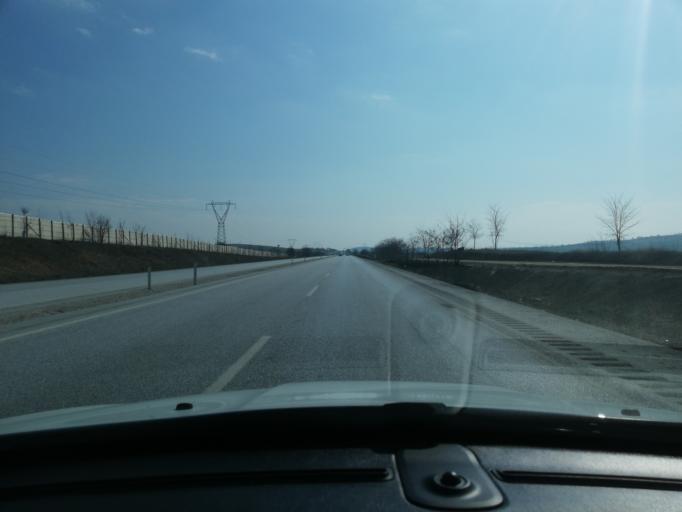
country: TR
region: Cankiri
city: Kursunlu
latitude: 40.8421
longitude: 33.1701
